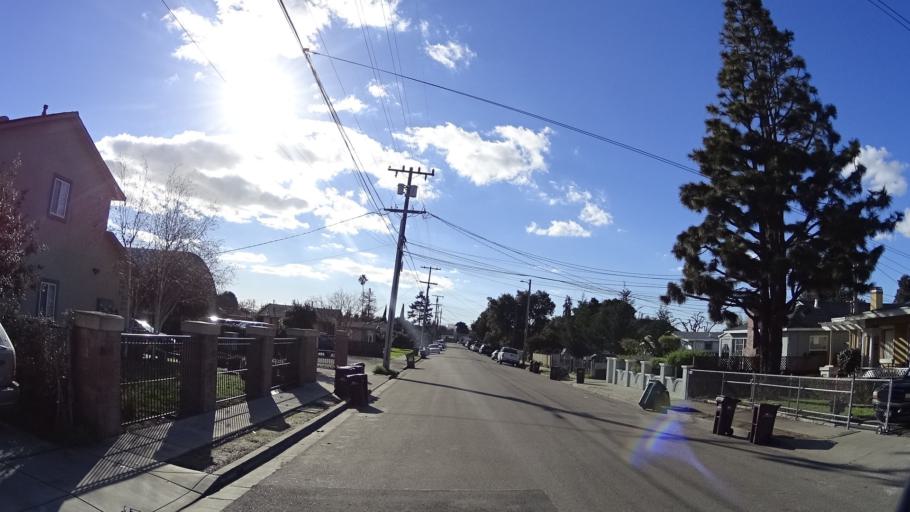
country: US
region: California
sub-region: Alameda County
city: Cherryland
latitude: 37.6704
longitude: -122.0991
